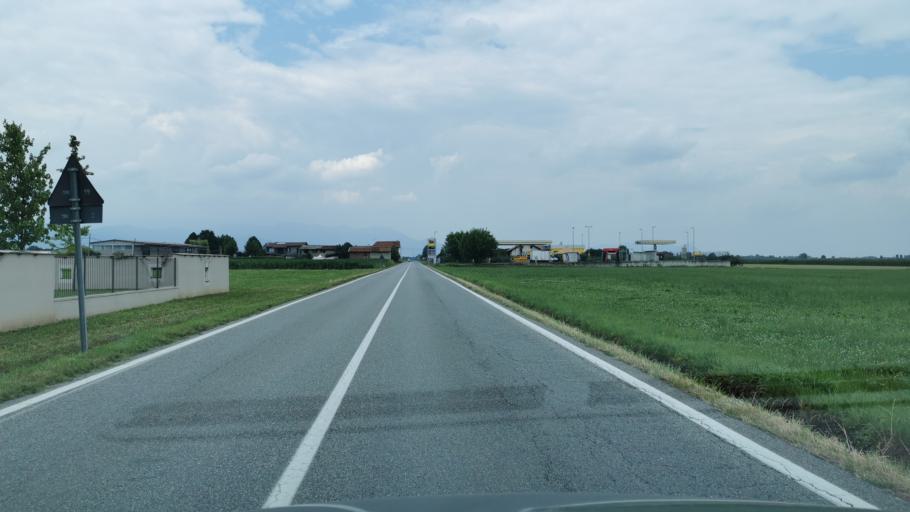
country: IT
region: Piedmont
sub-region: Provincia di Torino
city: Cavour
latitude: 44.8046
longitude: 7.3731
